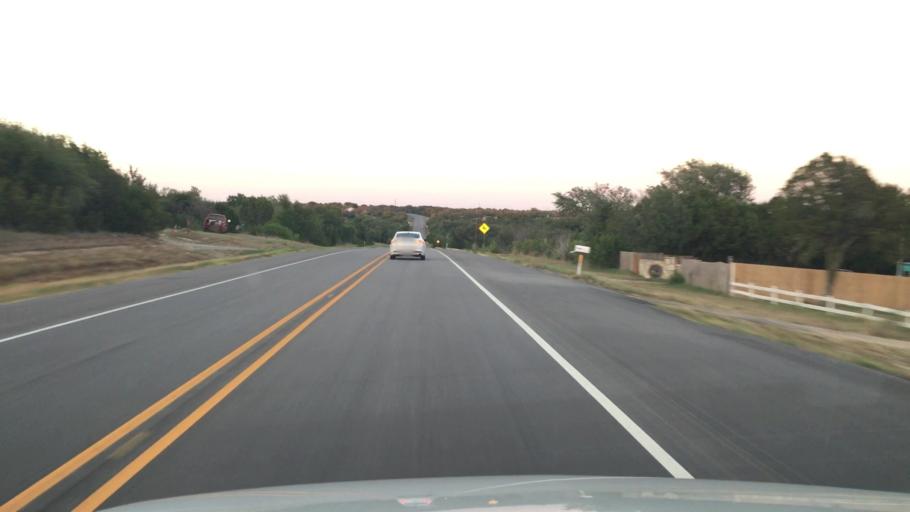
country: US
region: Texas
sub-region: Somervell County
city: Glen Rose
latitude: 32.1912
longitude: -97.8247
